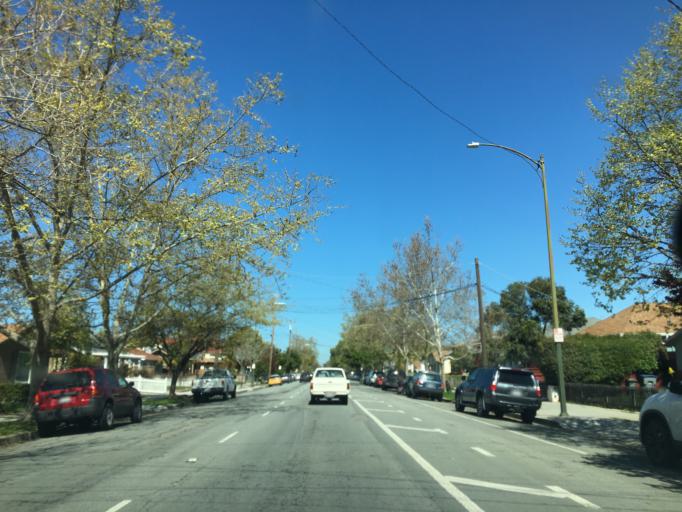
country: US
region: California
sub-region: Santa Clara County
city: San Jose
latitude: 37.3462
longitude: -121.8837
